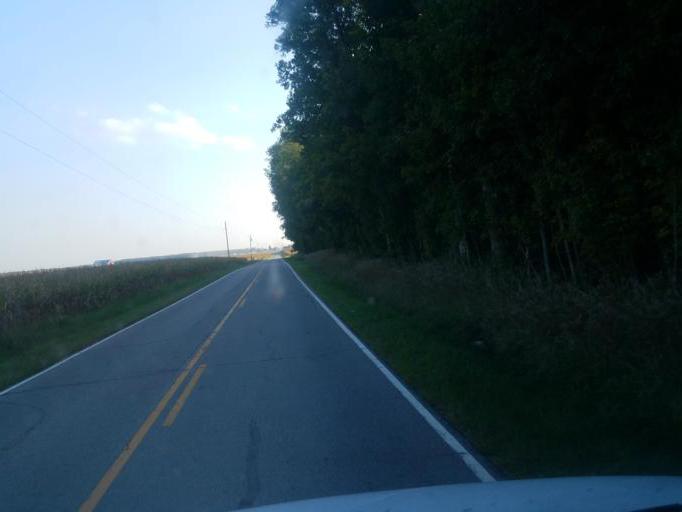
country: US
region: Ohio
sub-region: Crawford County
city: Bucyrus
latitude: 40.9035
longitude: -82.9018
